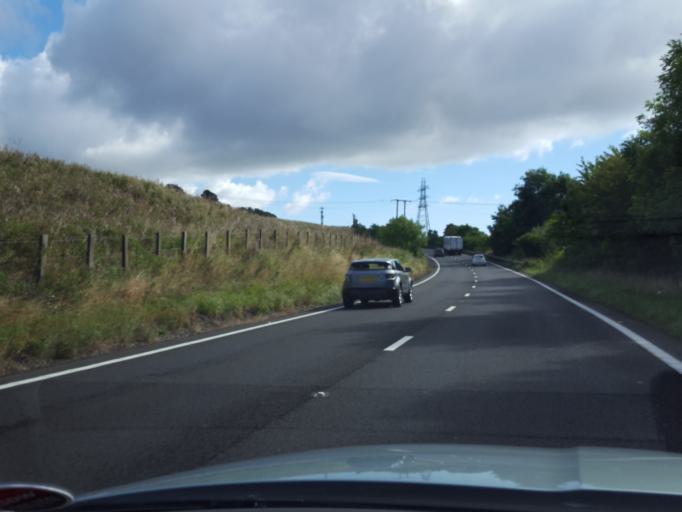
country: GB
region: Scotland
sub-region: Fife
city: Inverkeithing
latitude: 56.0452
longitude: -3.4114
